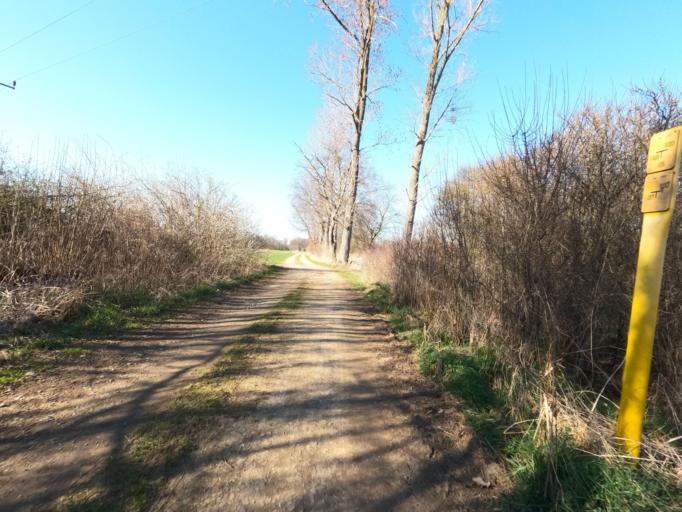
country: DE
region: North Rhine-Westphalia
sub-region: Regierungsbezirk Koln
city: Linnich
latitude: 50.9726
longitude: 6.2977
